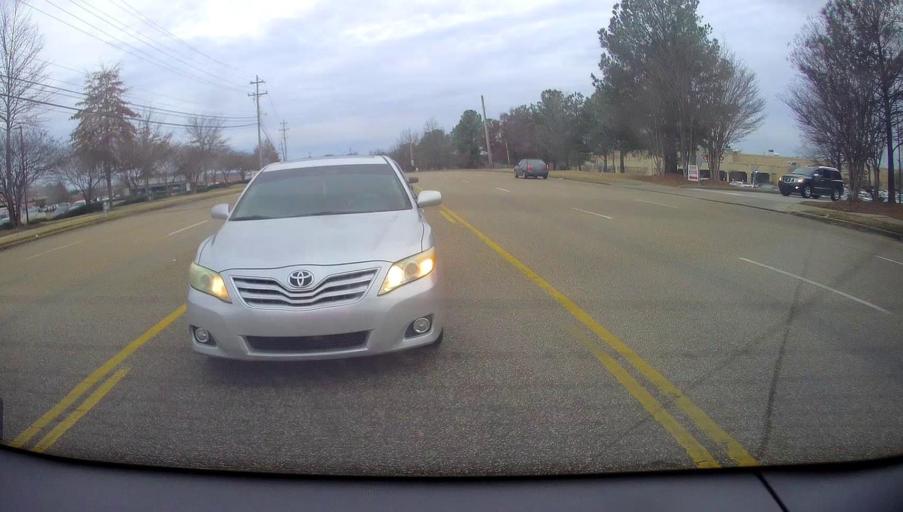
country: US
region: Tennessee
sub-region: Shelby County
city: Germantown
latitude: 35.0475
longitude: -89.7958
